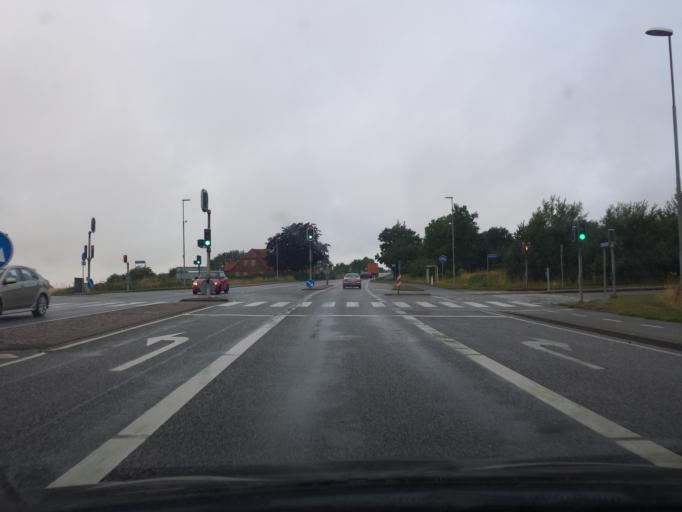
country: DK
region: South Denmark
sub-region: Sonderborg Kommune
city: Guderup
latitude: 54.9990
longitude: 9.8502
